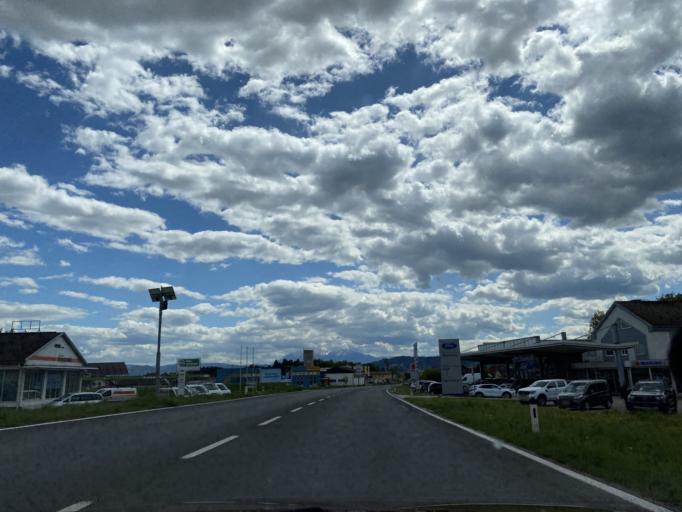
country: AT
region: Carinthia
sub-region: Politischer Bezirk Wolfsberg
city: Wolfsberg
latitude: 46.8163
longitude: 14.8353
